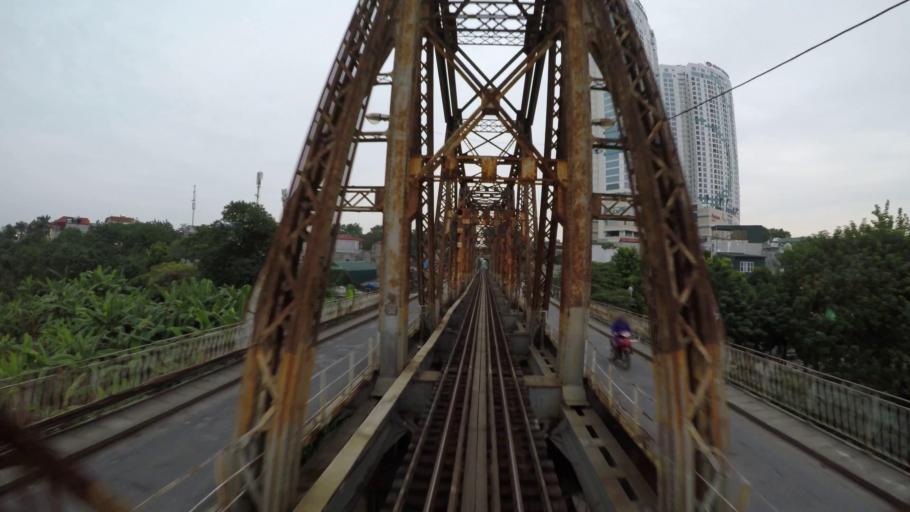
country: VN
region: Ha Noi
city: Hoan Kiem
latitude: 21.0518
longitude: 105.8903
